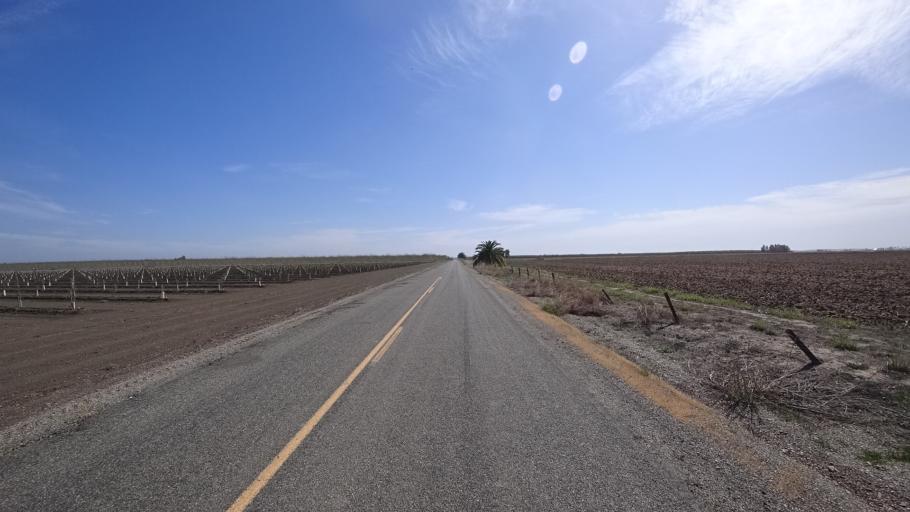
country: US
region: California
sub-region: Glenn County
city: Hamilton City
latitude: 39.6161
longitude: -122.0543
